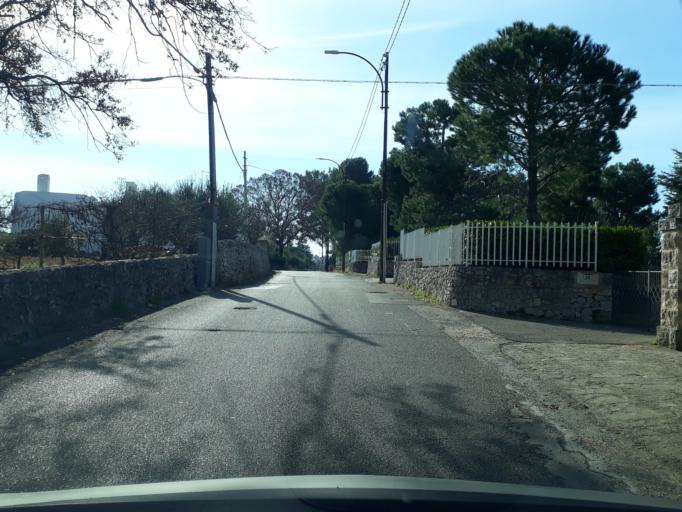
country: IT
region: Apulia
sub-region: Provincia di Brindisi
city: Lamie di Olimpie-Selva
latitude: 40.7944
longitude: 17.3540
